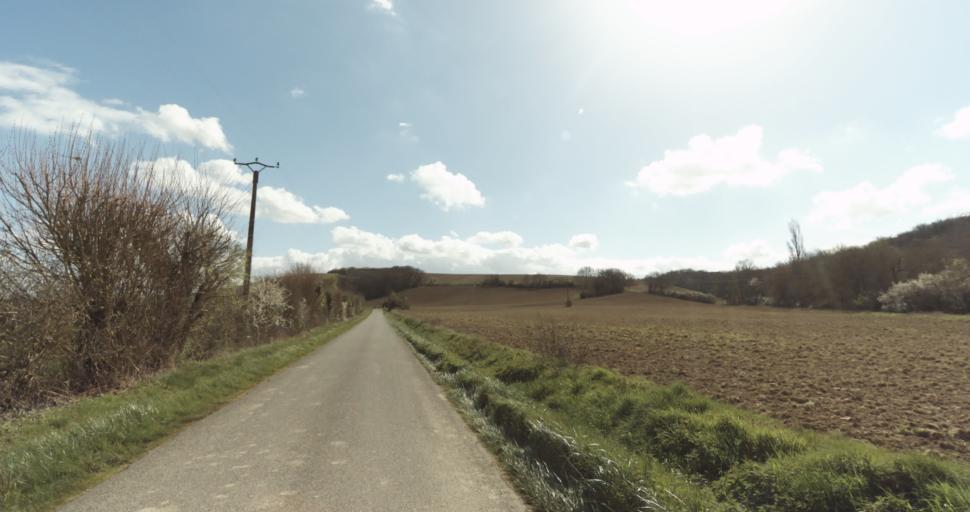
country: FR
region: Midi-Pyrenees
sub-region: Departement de la Haute-Garonne
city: Auterive
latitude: 43.3740
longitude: 1.5136
